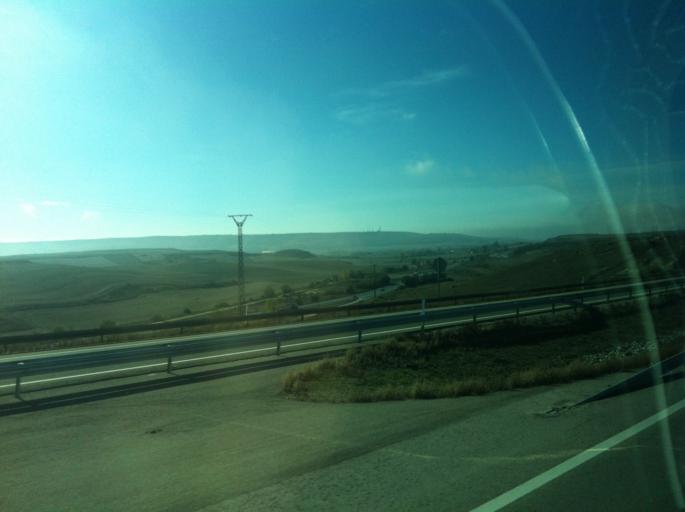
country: ES
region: Castille and Leon
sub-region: Provincia de Burgos
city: Fresno de Rodilla
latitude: 42.4250
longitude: -3.5108
